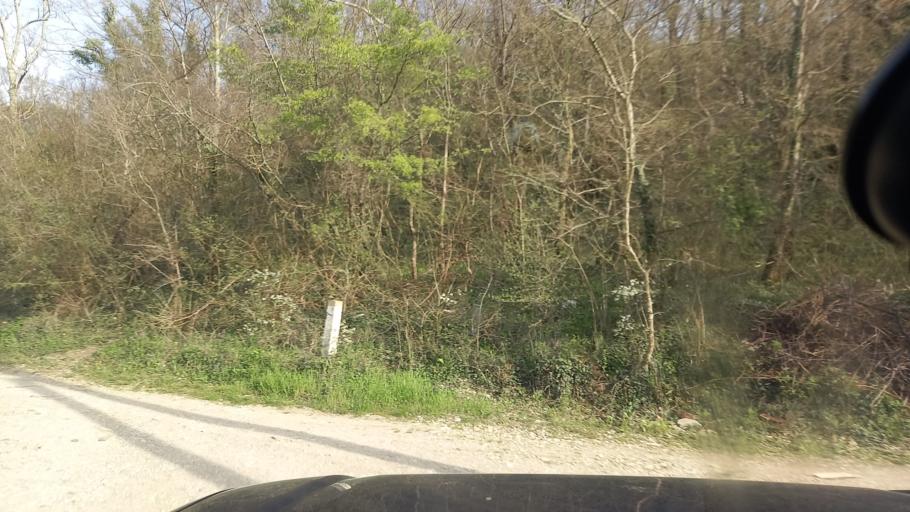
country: RU
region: Krasnodarskiy
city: Arkhipo-Osipovka
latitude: 44.3661
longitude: 38.5475
